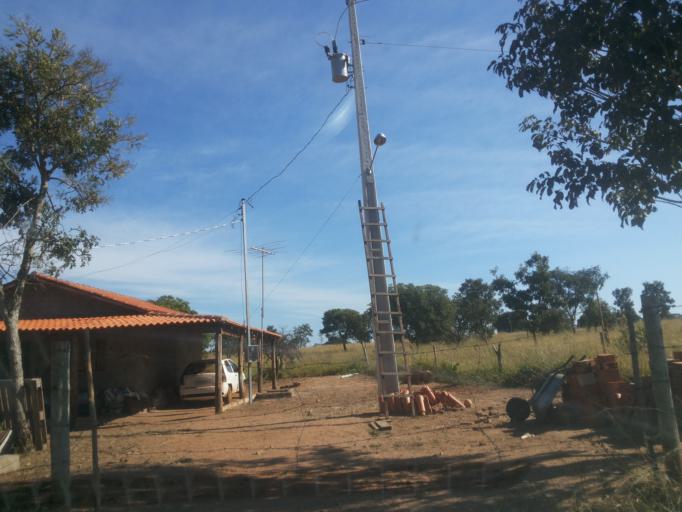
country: BR
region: Minas Gerais
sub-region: Ituiutaba
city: Ituiutaba
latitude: -19.1224
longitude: -49.3828
